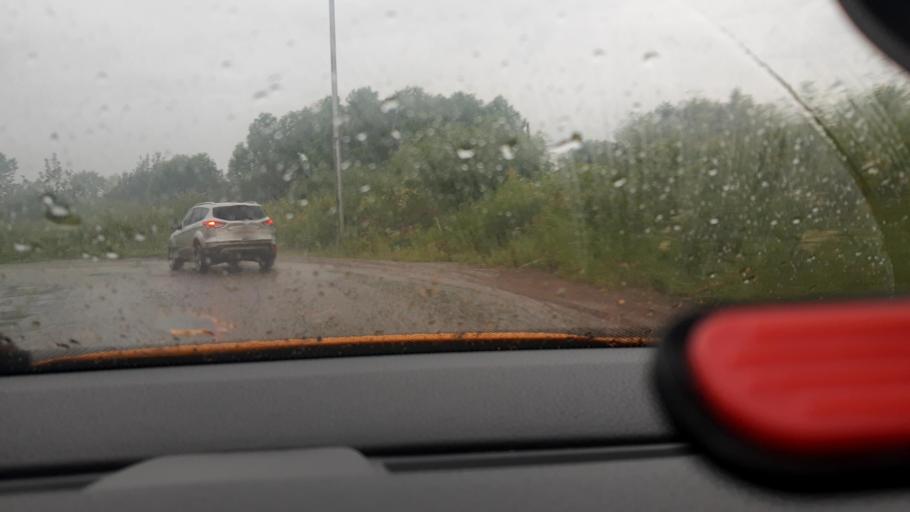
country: RU
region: Moskovskaya
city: Novopodrezkovo
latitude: 55.9399
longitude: 37.3743
